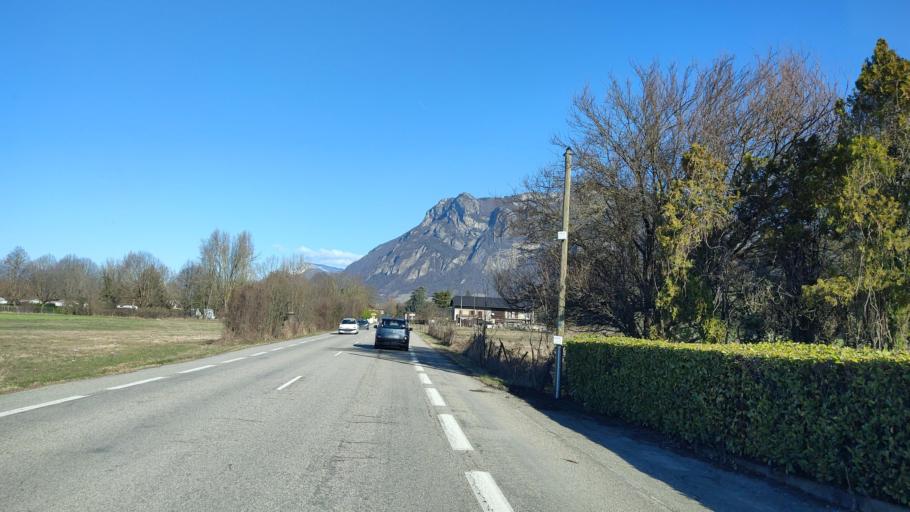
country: FR
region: Rhone-Alpes
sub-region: Departement de la Savoie
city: Montmelian
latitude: 45.4752
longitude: 6.0419
